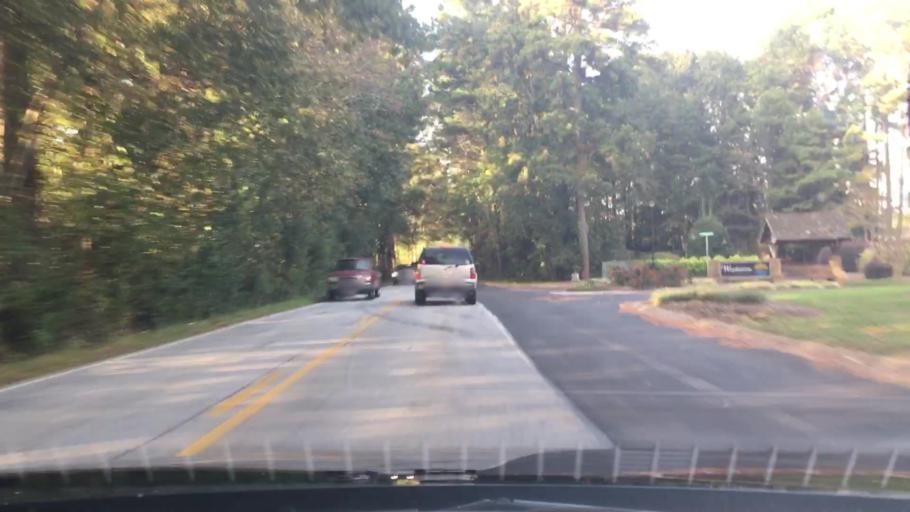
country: US
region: Georgia
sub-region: Coweta County
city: East Newnan
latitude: 33.3829
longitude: -84.7145
